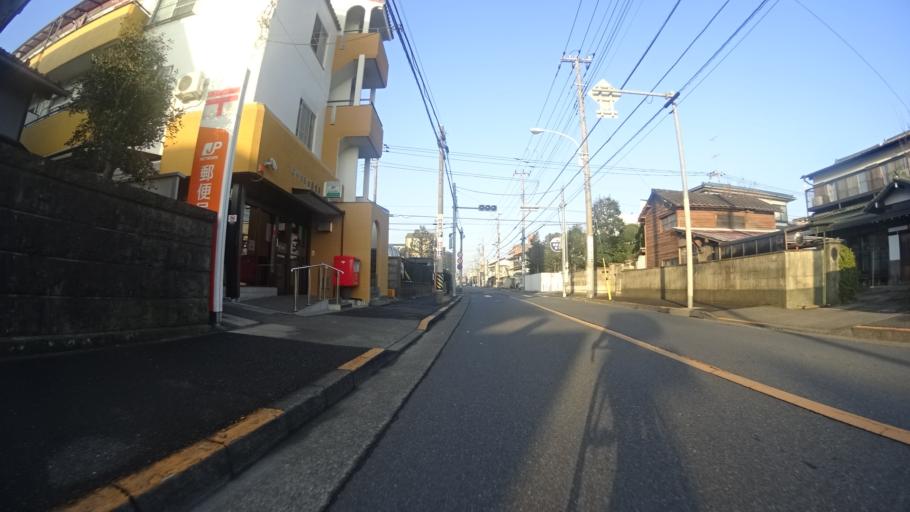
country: JP
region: Tokyo
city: Chofugaoka
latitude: 35.6678
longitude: 139.5100
